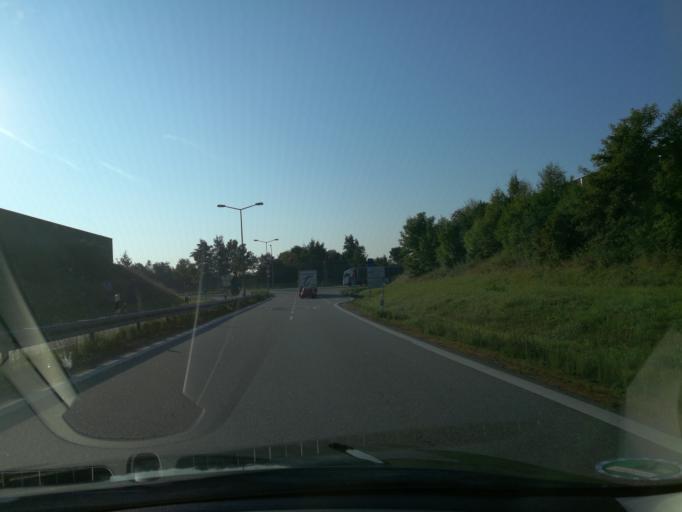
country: DE
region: Bavaria
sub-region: Upper Palatinate
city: Regensburg
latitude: 48.9945
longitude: 12.1314
